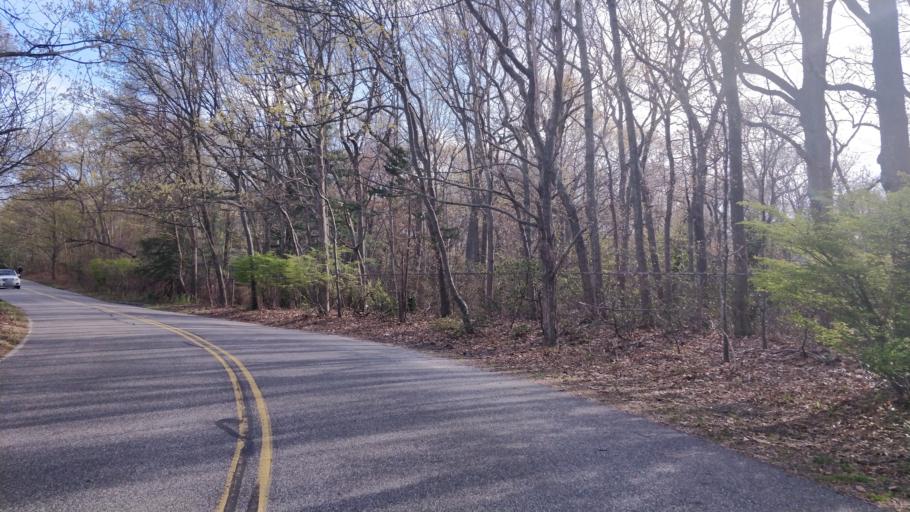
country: US
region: New York
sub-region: Suffolk County
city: Stony Brook
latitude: 40.9565
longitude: -73.1366
